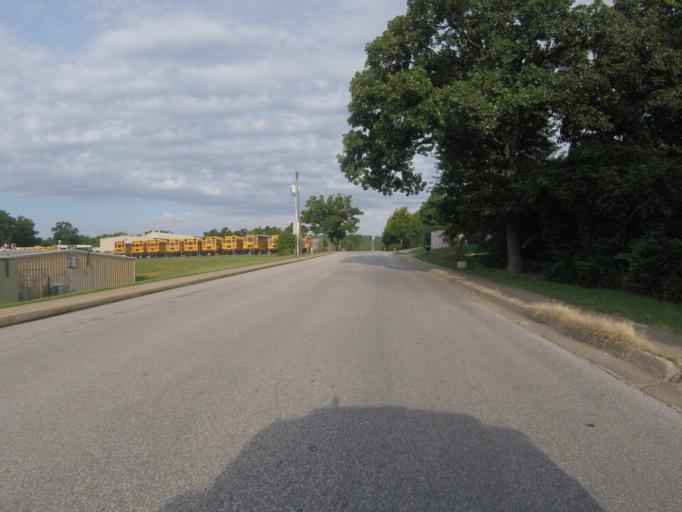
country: US
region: Arkansas
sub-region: Washington County
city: Fayetteville
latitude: 36.0599
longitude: -94.1911
